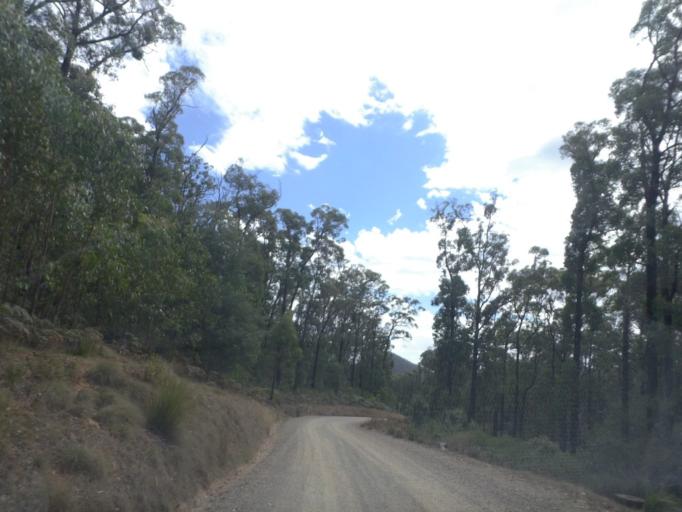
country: AU
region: Victoria
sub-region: Murrindindi
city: Alexandra
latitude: -37.4507
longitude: 145.7574
